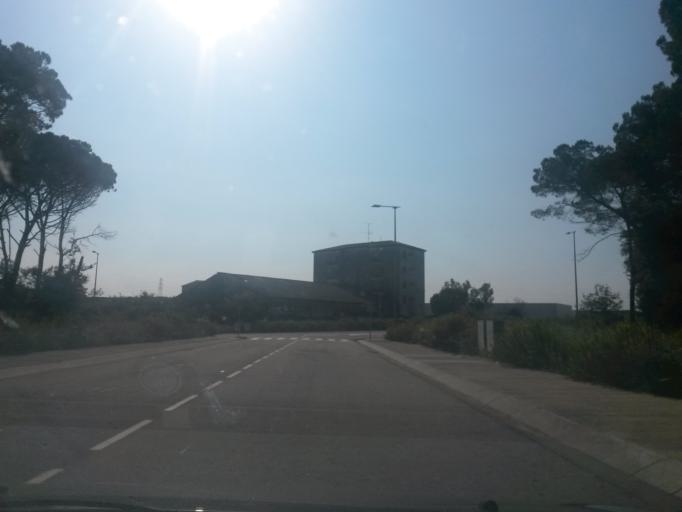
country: ES
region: Catalonia
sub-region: Provincia de Girona
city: Fornells de la Selva
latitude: 41.9443
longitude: 2.8021
